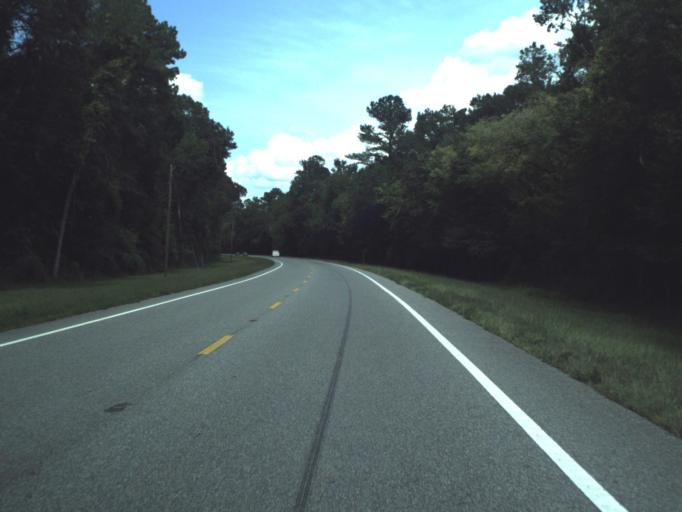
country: US
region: Florida
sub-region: Hernando County
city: Ridge Manor
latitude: 28.5084
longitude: -82.1145
